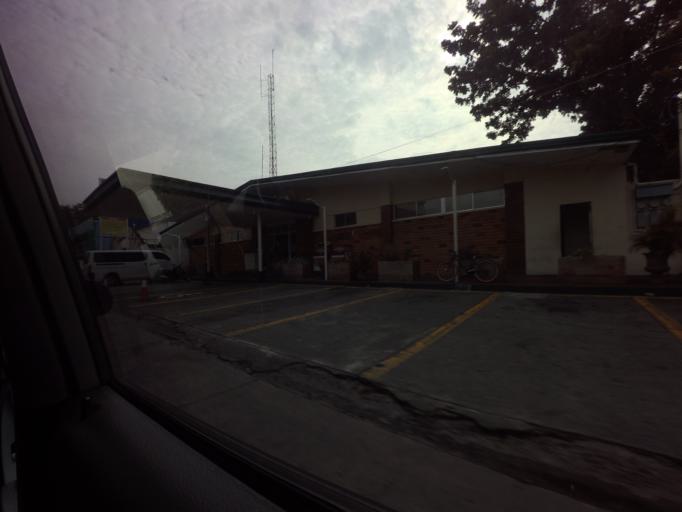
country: PH
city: Sambayanihan People's Village
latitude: 14.4463
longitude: 121.0266
